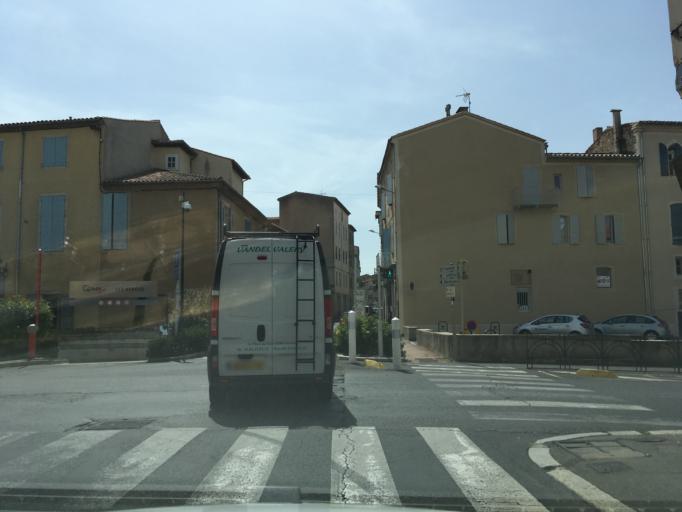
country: FR
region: Midi-Pyrenees
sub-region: Departement du Tarn
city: Castres
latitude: 43.6077
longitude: 2.2420
